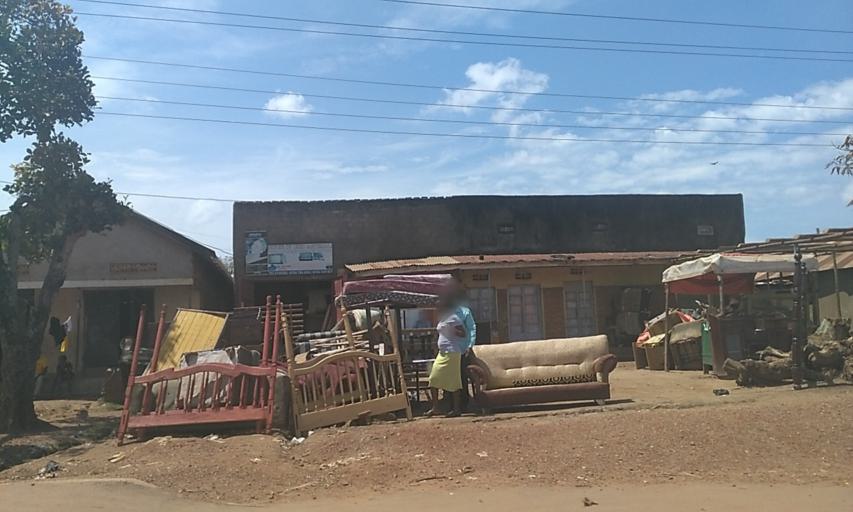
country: UG
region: Central Region
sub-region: Wakiso District
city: Wakiso
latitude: 0.3813
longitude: 32.5190
